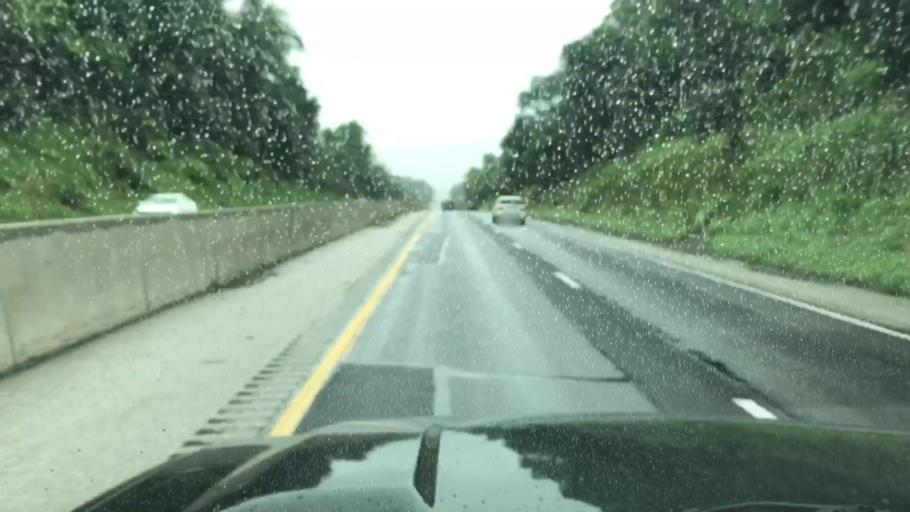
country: US
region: Pennsylvania
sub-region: York County
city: Emigsville
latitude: 40.0068
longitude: -76.7388
